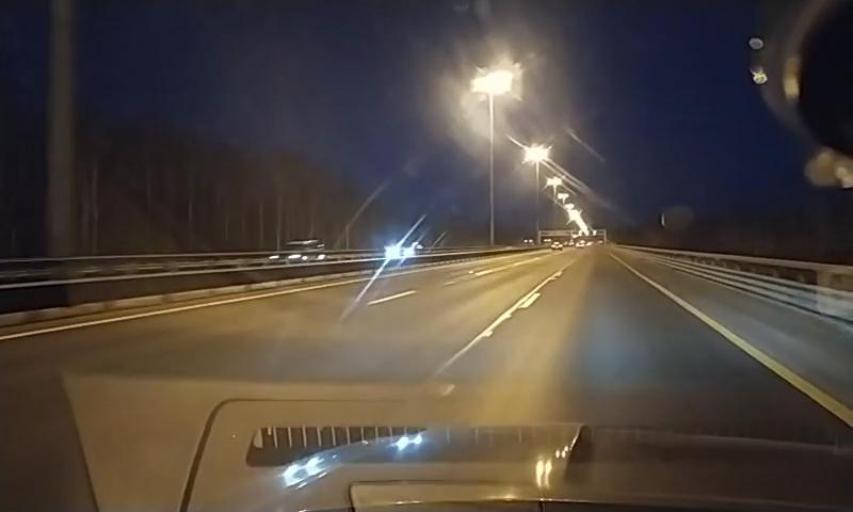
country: RU
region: St.-Petersburg
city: Pesochnyy
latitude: 60.0995
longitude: 30.0916
